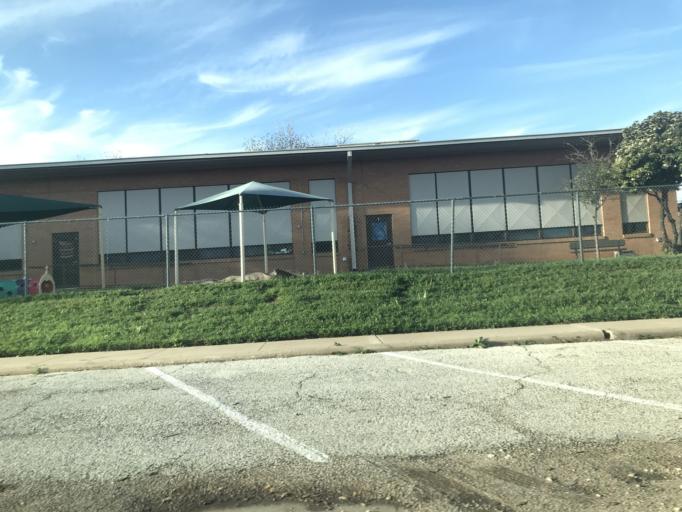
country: US
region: Texas
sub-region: Taylor County
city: Abilene
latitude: 32.4341
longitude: -99.7629
